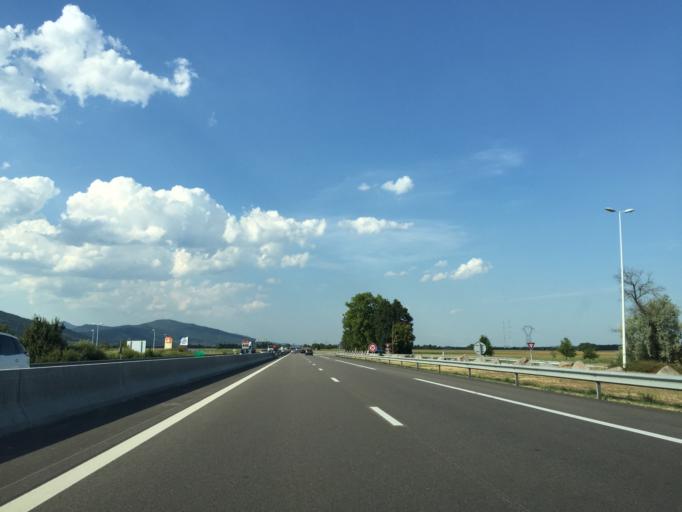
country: FR
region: Alsace
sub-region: Departement du Bas-Rhin
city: Kintzheim
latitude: 48.2323
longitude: 7.4072
